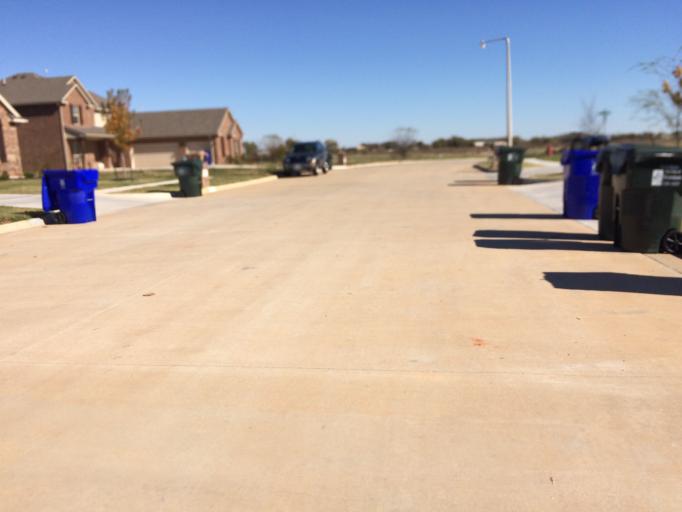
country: US
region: Oklahoma
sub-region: Cleveland County
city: Noble
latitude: 35.1719
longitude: -97.4205
